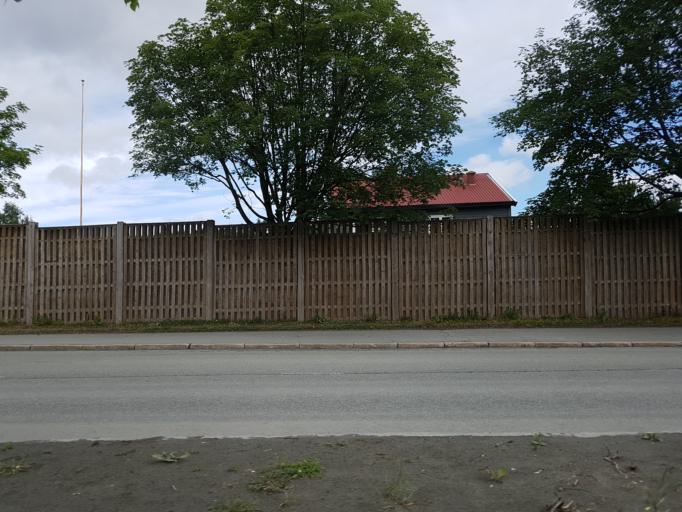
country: NO
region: Sor-Trondelag
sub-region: Trondheim
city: Trondheim
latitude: 63.4064
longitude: 10.4246
